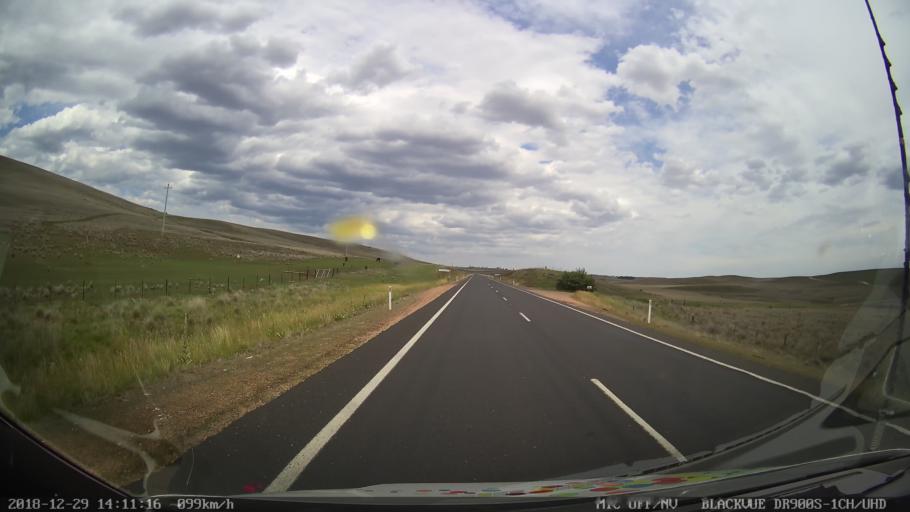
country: AU
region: New South Wales
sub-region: Cooma-Monaro
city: Cooma
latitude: -36.4035
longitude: 149.2193
